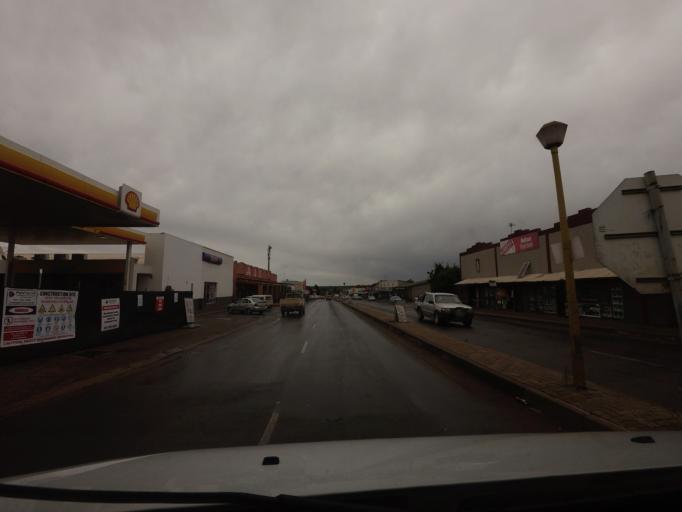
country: ZA
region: Mpumalanga
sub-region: Nkangala District Municipality
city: Belfast
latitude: -25.6956
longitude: 30.0431
